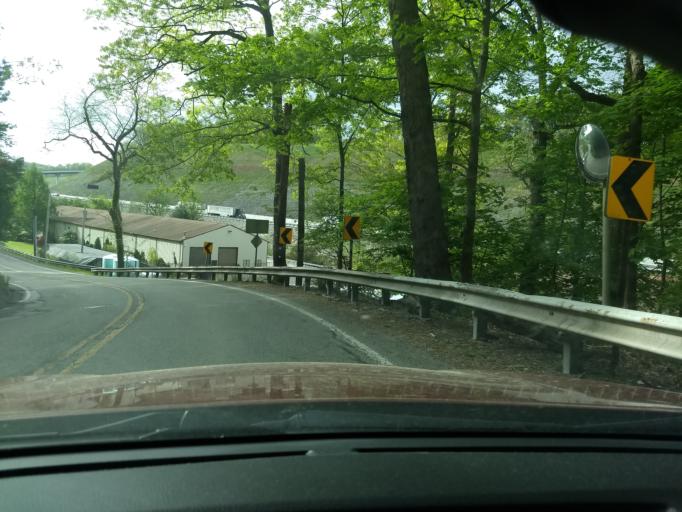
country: US
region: Pennsylvania
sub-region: Allegheny County
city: Russellton
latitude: 40.5868
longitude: -79.8828
